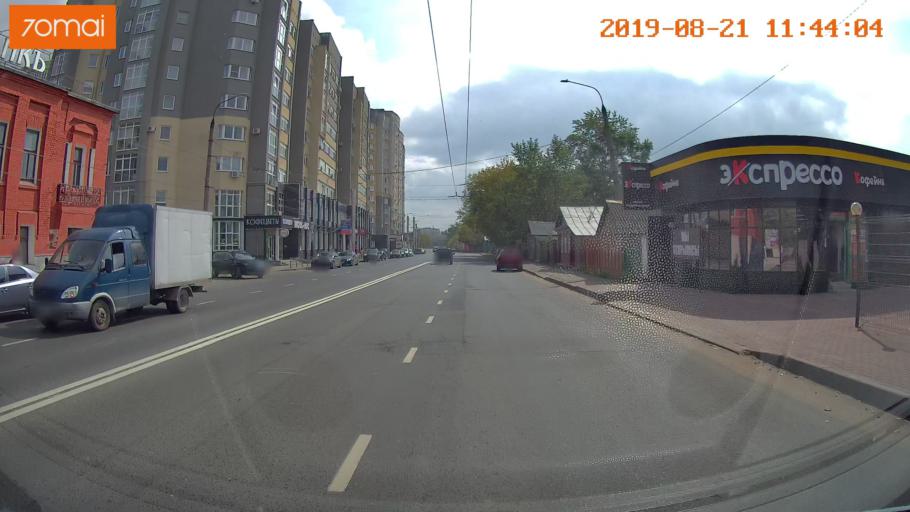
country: RU
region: Ivanovo
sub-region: Gorod Ivanovo
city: Ivanovo
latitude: 57.0048
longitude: 40.9699
